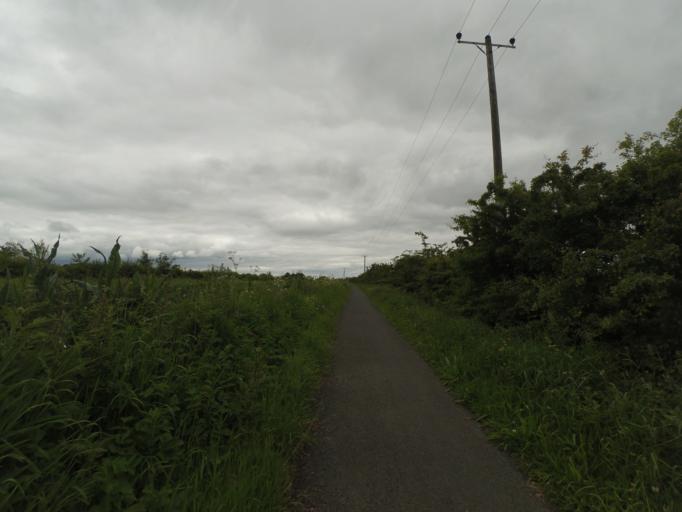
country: GB
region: Scotland
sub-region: West Lothian
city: Linlithgow
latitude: 55.9770
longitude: -3.5489
